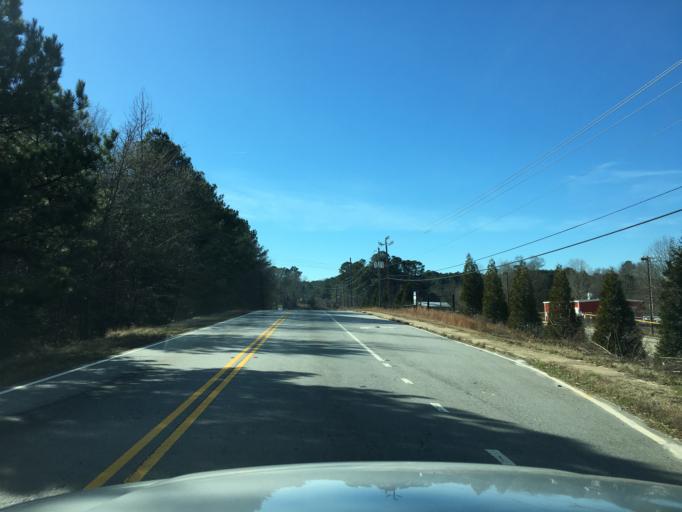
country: US
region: Georgia
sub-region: Rockdale County
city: Lakeview Estates
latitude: 33.6875
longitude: -84.0301
